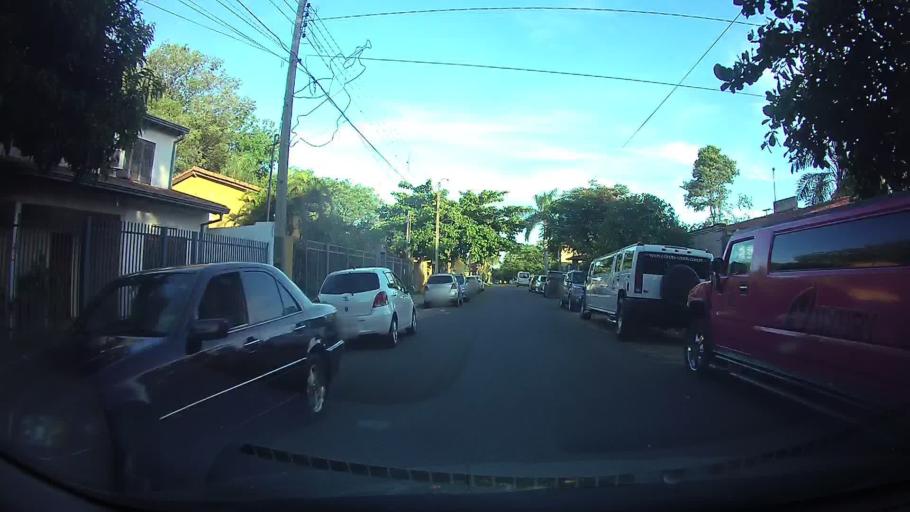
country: PY
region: Central
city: San Lorenzo
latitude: -25.2655
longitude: -57.5086
